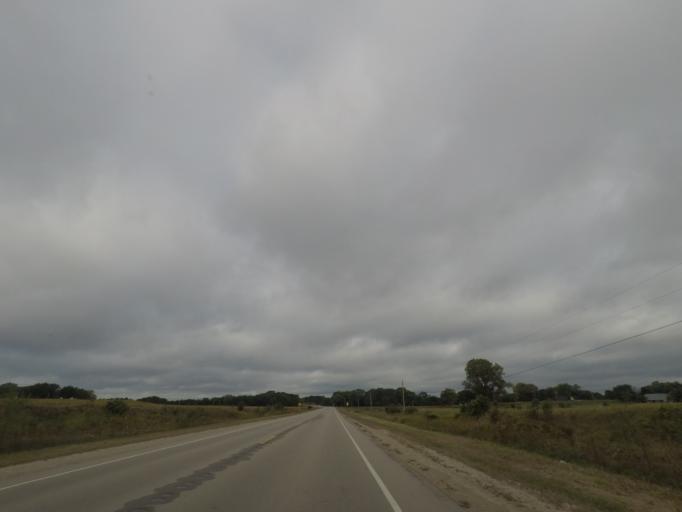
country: US
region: Wisconsin
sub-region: Jefferson County
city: Lake Ripley
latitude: 43.0107
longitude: -88.9595
